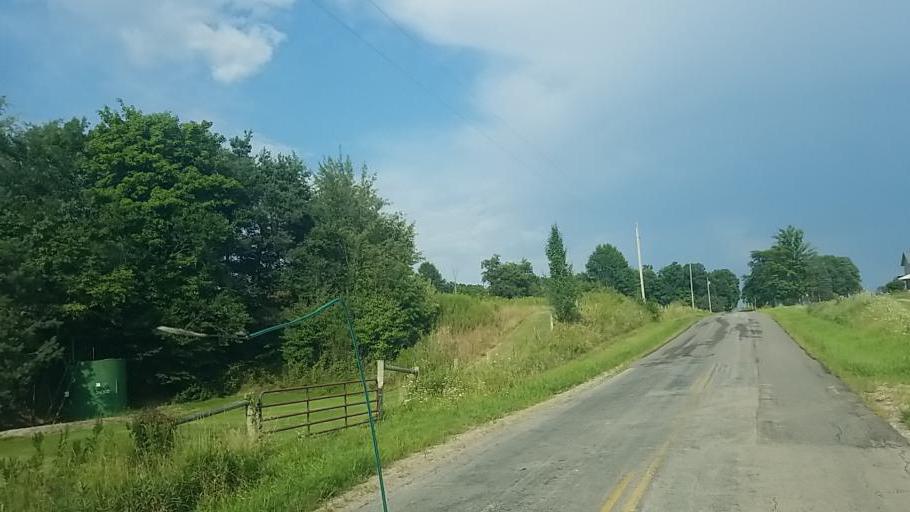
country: US
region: Ohio
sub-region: Wayne County
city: Smithville
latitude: 40.9159
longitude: -81.9023
